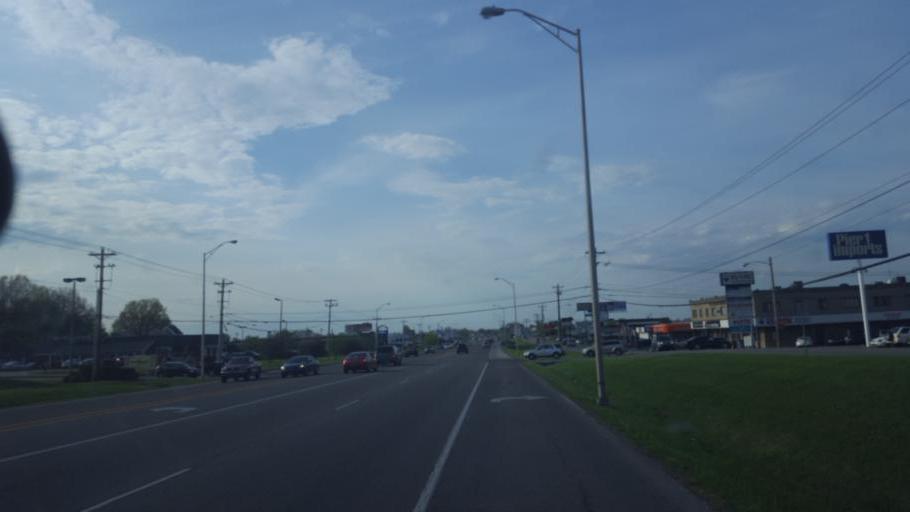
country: US
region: Kentucky
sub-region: Warren County
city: Bowling Green
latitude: 36.9504
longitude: -86.4250
